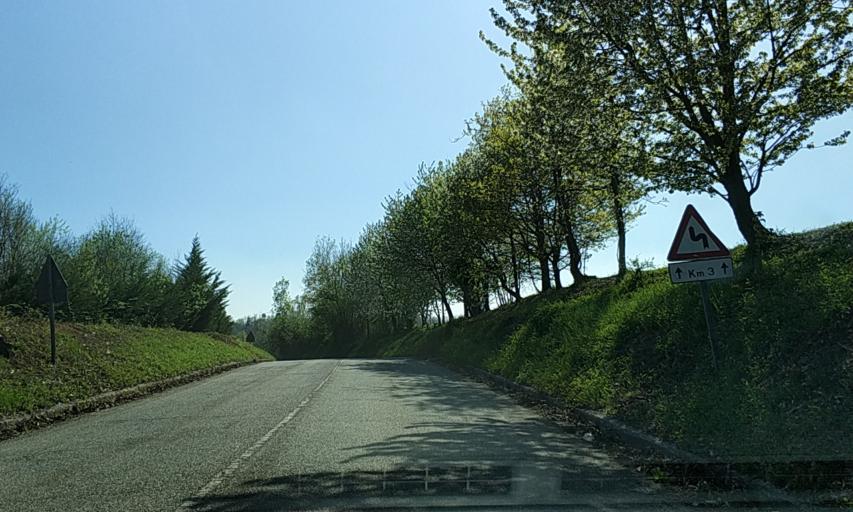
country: IT
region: Piedmont
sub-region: Provincia di Torino
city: Vauda Canavese Superiore
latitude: 45.2893
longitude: 7.6212
